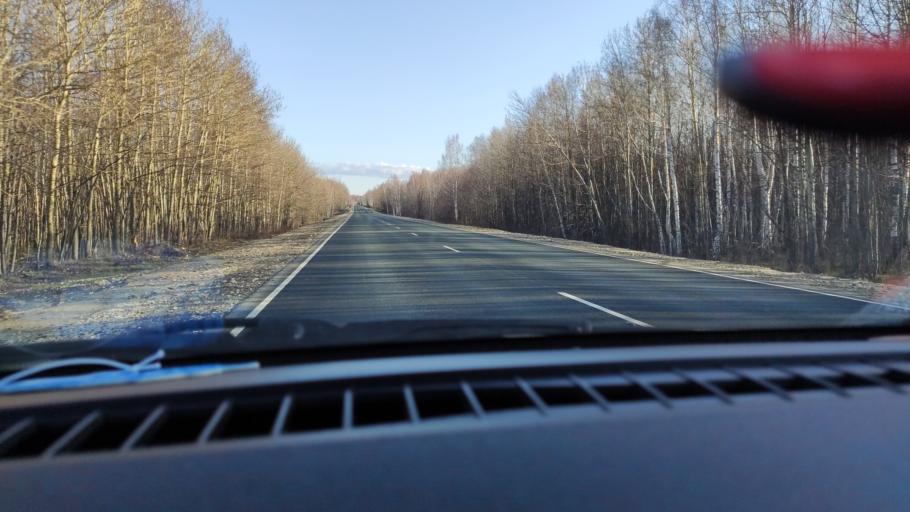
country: RU
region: Saratov
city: Khvalynsk
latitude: 52.4304
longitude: 48.0088
